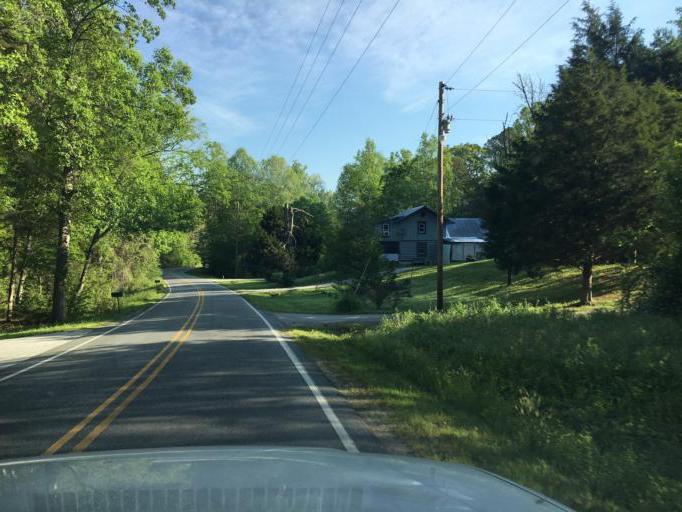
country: US
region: North Carolina
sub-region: Rutherford County
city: Rutherfordton
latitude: 35.2995
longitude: -82.0056
